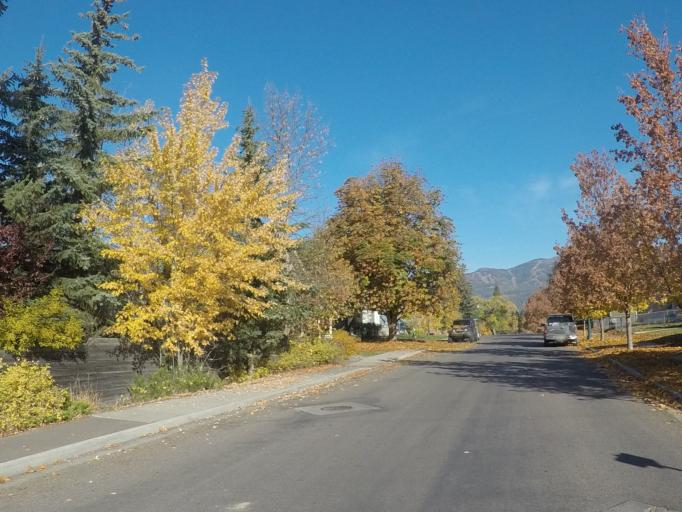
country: US
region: Montana
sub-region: Flathead County
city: Whitefish
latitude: 48.4153
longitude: -114.3507
